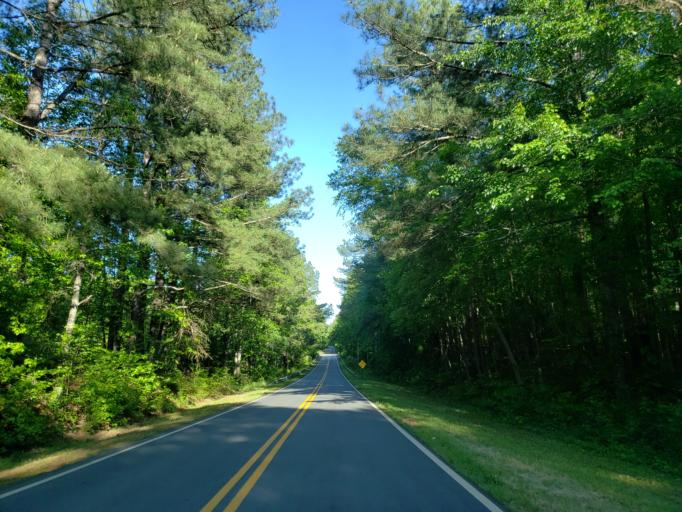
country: US
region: Georgia
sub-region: Haralson County
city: Tallapoosa
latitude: 33.7961
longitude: -85.2706
